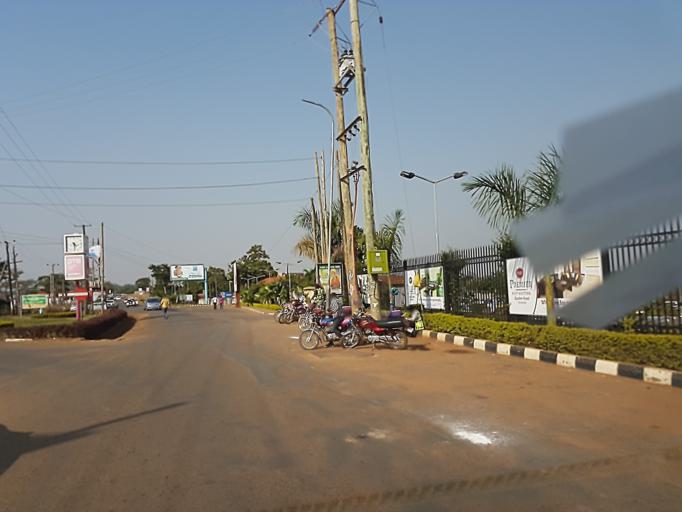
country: UG
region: Central Region
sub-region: Wakiso District
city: Entebbe
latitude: 0.0665
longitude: 32.4758
